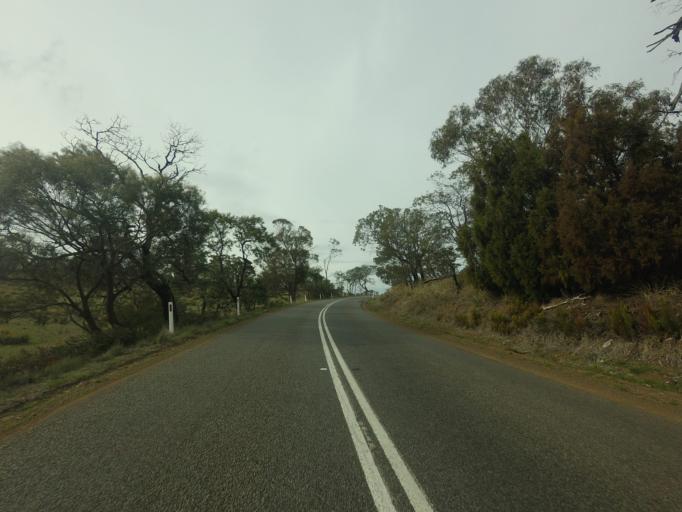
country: AU
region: Tasmania
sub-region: Sorell
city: Sorell
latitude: -42.3027
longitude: 147.9707
